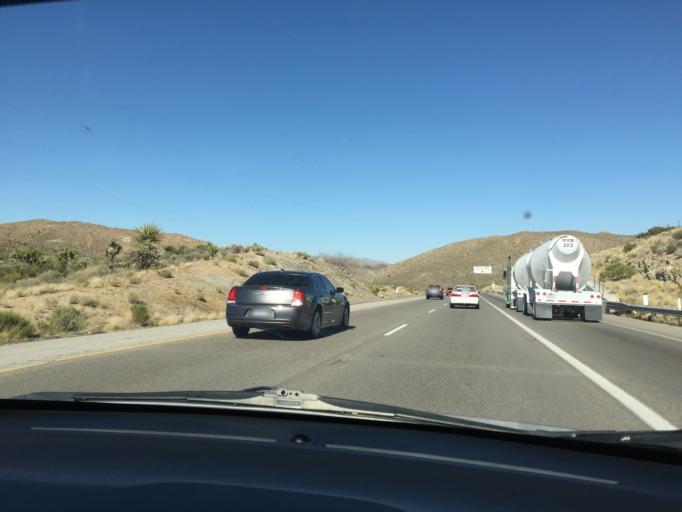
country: US
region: Nevada
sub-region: Clark County
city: Sandy Valley
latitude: 35.4677
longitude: -115.5186
